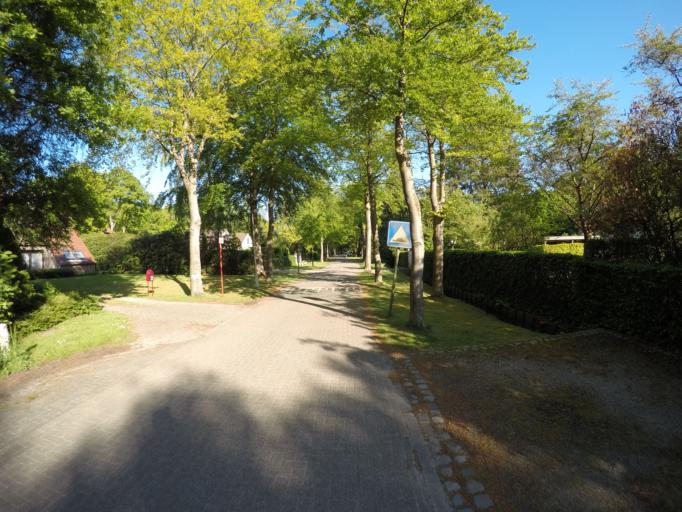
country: BE
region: Flanders
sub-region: Provincie Antwerpen
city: Schilde
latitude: 51.2524
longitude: 4.6215
